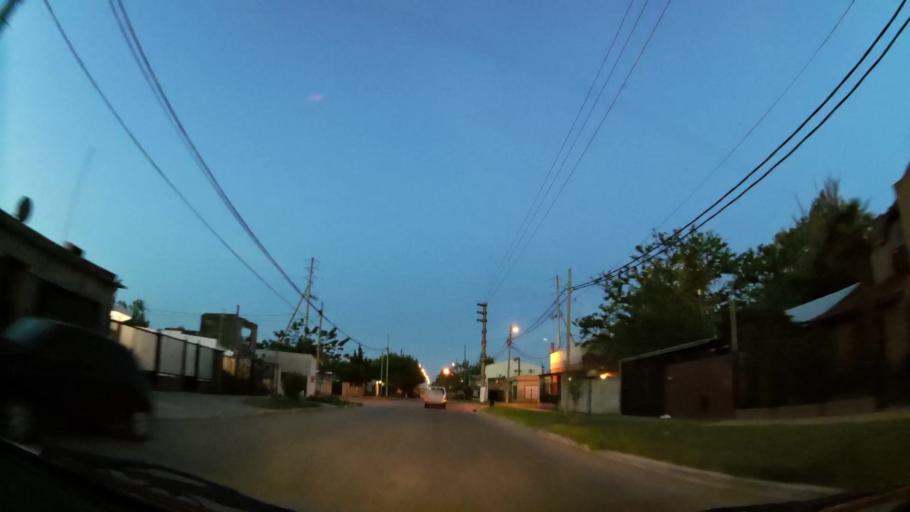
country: AR
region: Buenos Aires
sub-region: Partido de Quilmes
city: Quilmes
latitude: -34.7605
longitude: -58.1912
